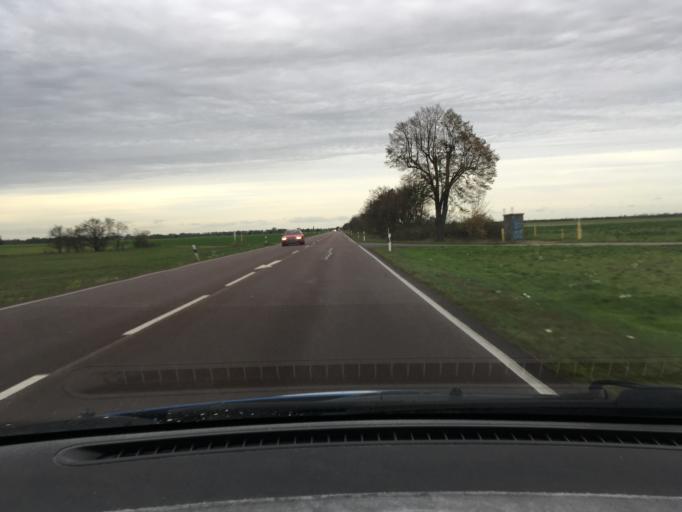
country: DE
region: Saxony-Anhalt
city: Zerbst
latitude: 51.9793
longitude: 12.0596
